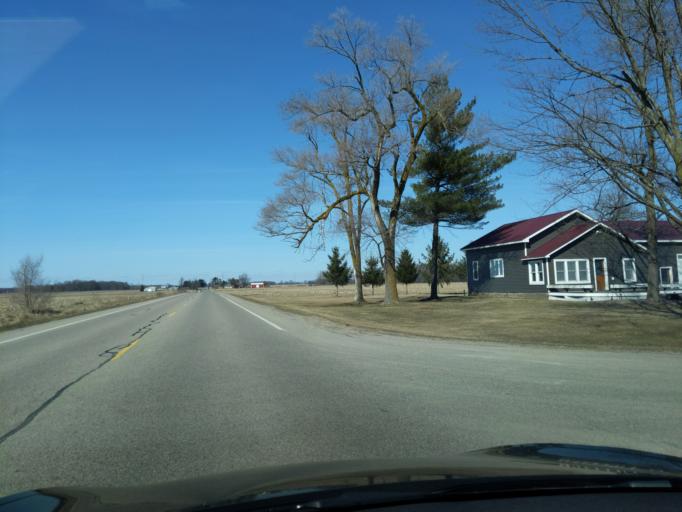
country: US
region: Michigan
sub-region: Ionia County
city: Lake Odessa
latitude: 42.8138
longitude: -85.1337
